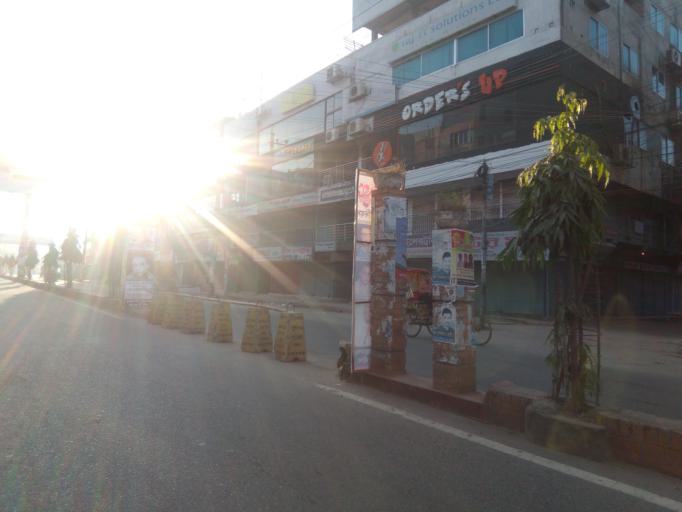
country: BD
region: Rajshahi
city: Rajshahi
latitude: 24.3652
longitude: 88.6011
